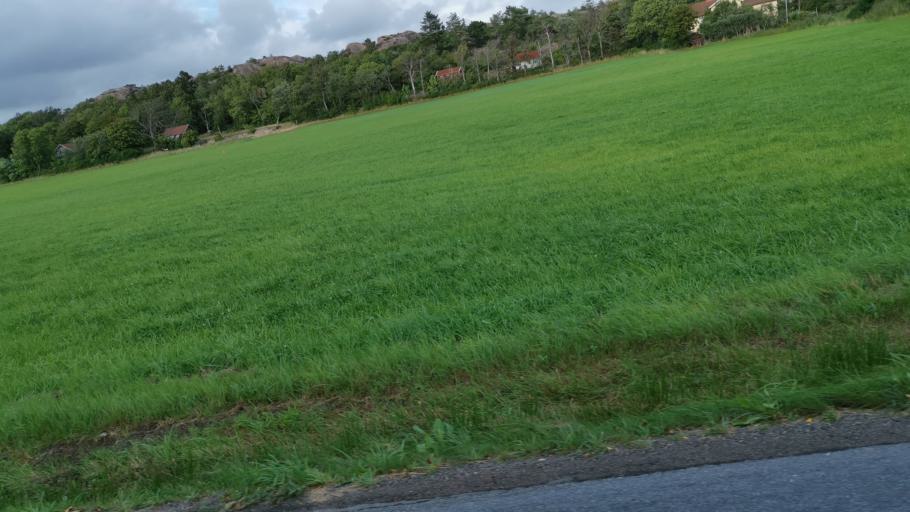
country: SE
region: Vaestra Goetaland
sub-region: Sotenas Kommun
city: Hunnebostrand
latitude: 58.5166
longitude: 11.3068
